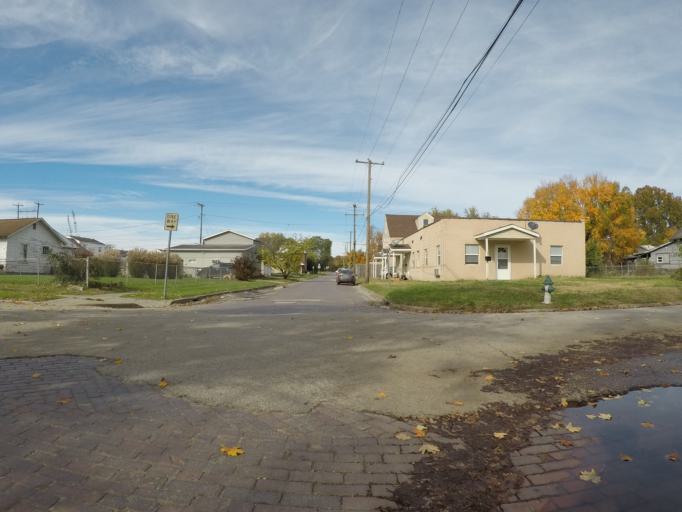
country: US
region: Ohio
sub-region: Lawrence County
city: Burlington
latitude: 38.4001
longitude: -82.5024
